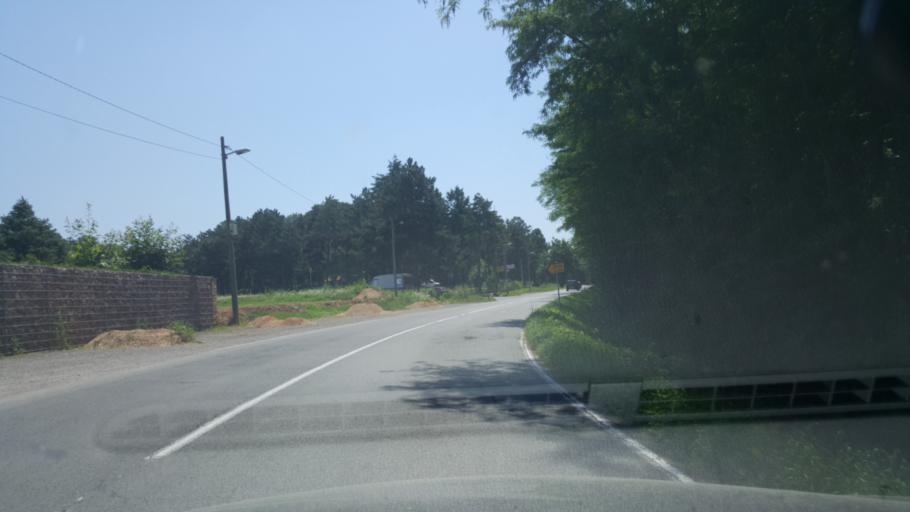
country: RS
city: Rusanj
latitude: 44.6810
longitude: 20.5164
